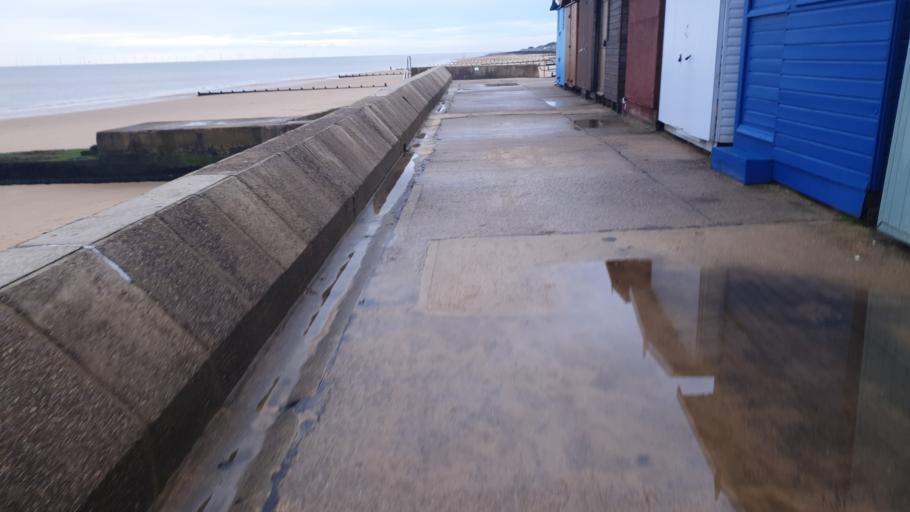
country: GB
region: England
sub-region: Essex
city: Walton-on-the-Naze
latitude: 51.8364
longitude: 1.2583
